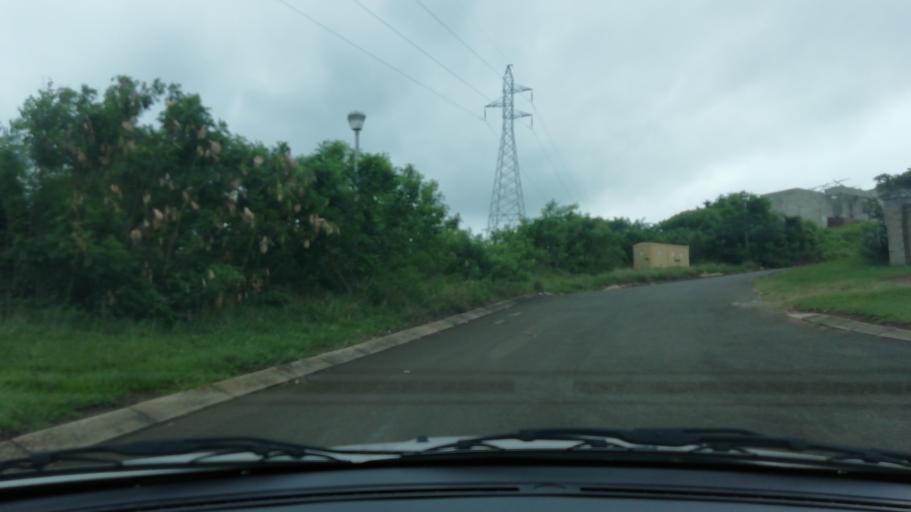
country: ZA
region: KwaZulu-Natal
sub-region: uThungulu District Municipality
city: Empangeni
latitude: -28.7597
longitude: 31.8845
